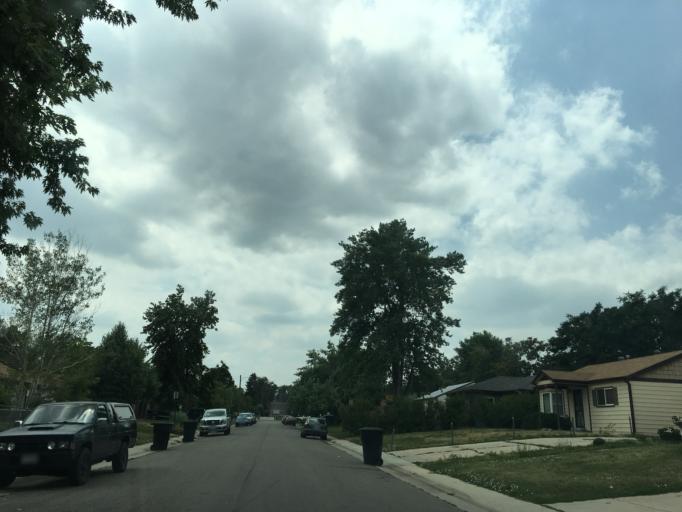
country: US
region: Colorado
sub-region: Arapahoe County
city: Sheridan
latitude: 39.6804
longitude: -105.0333
